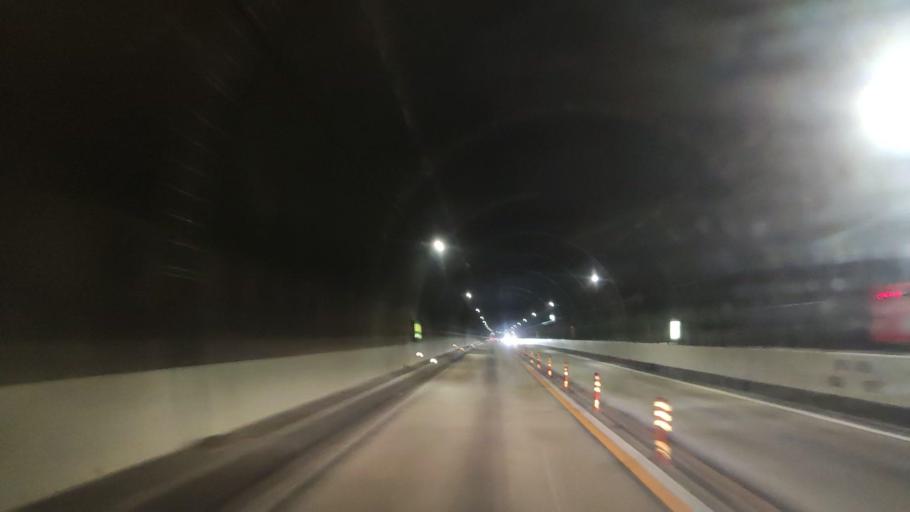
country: JP
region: Hiroshima
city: Innoshima
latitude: 34.1785
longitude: 133.0682
